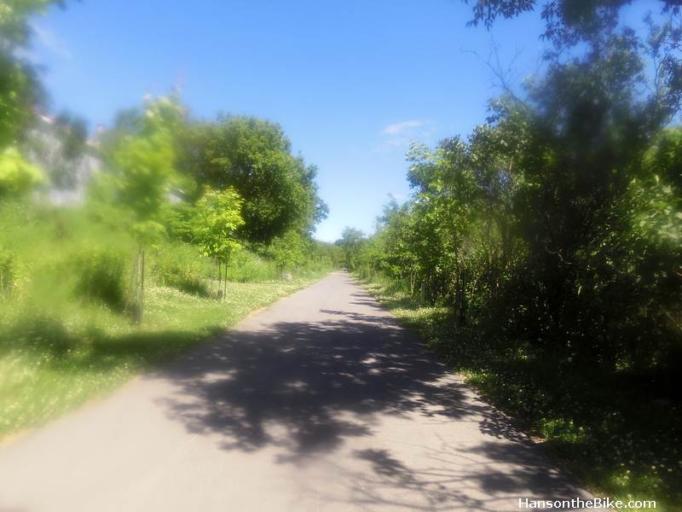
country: CA
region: Ontario
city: Kingston
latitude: 44.2458
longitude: -76.4843
